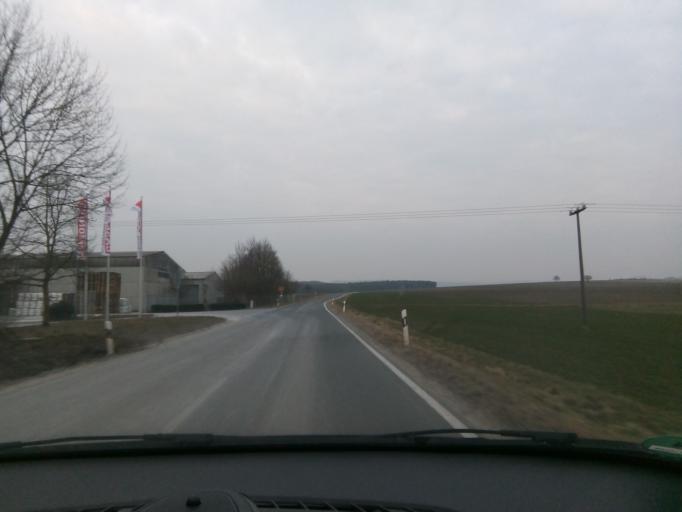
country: DE
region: Bavaria
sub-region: Regierungsbezirk Unterfranken
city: Sulzheim
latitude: 49.9486
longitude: 10.3453
